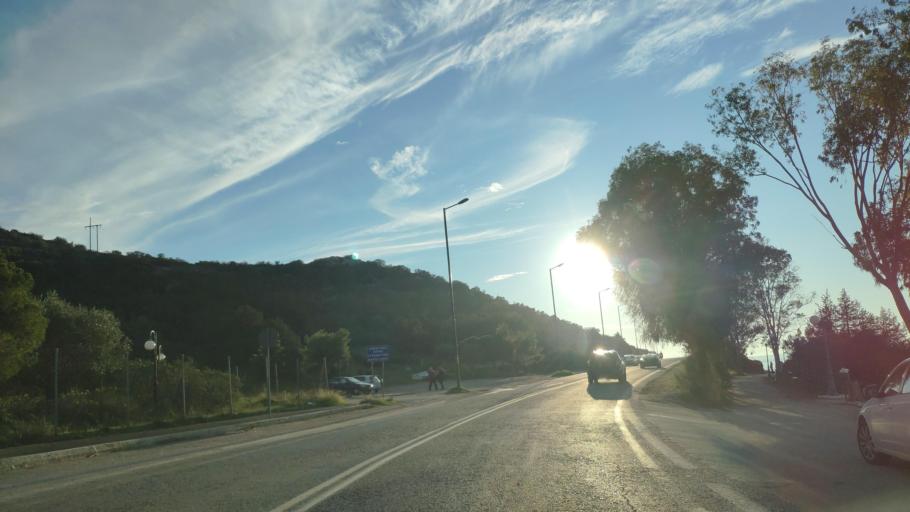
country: GR
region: Attica
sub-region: Nomarchia Anatolikis Attikis
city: Palaia Fokaia
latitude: 37.7146
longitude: 23.9458
